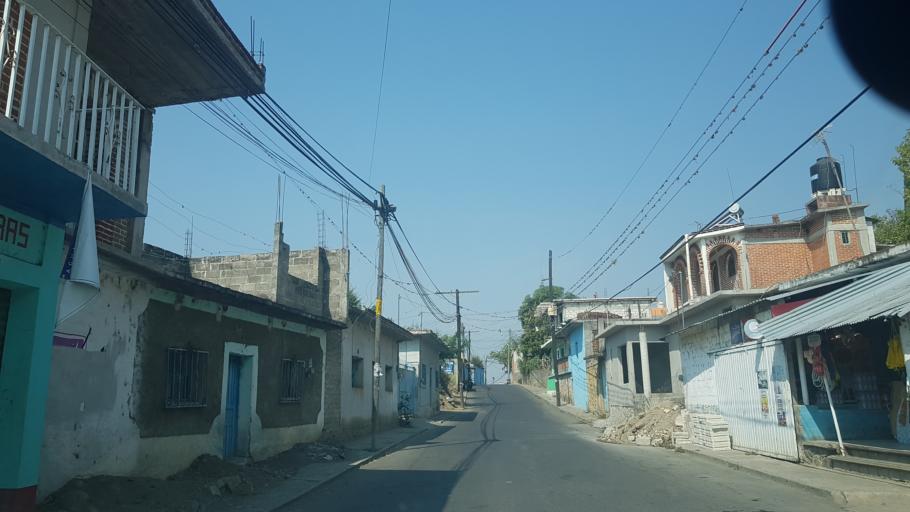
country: MX
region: Morelos
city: Tlacotepec
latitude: 18.8162
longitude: -98.7482
